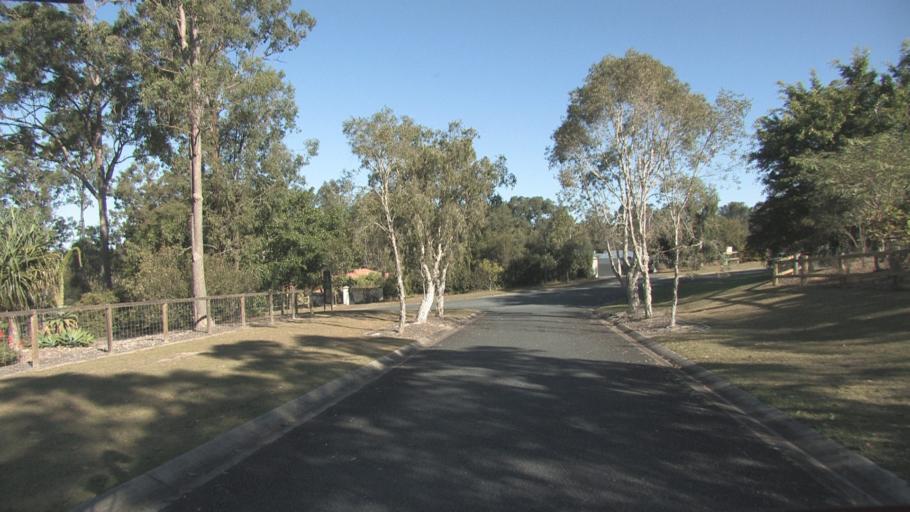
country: AU
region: Queensland
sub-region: Ipswich
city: Springfield Lakes
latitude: -27.7369
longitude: 152.9212
